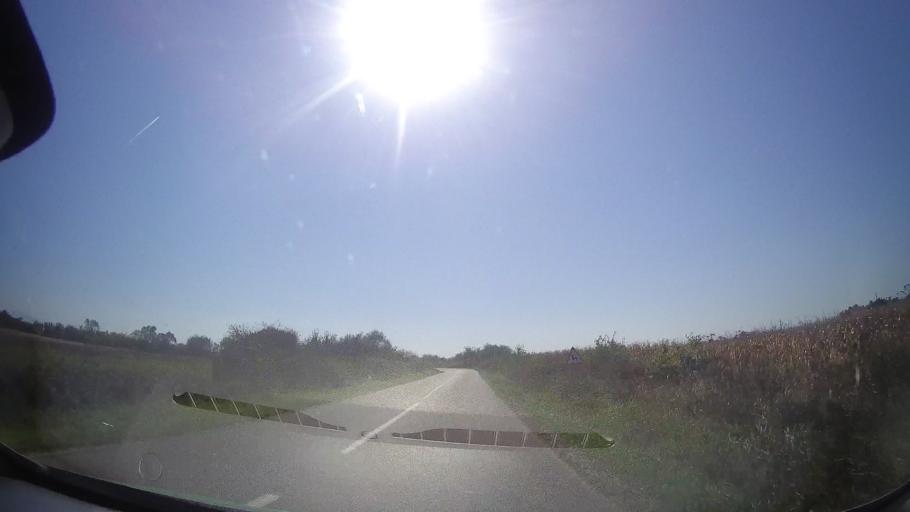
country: RO
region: Timis
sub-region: Comuna Bethausen
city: Bethausen
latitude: 45.8230
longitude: 21.9596
